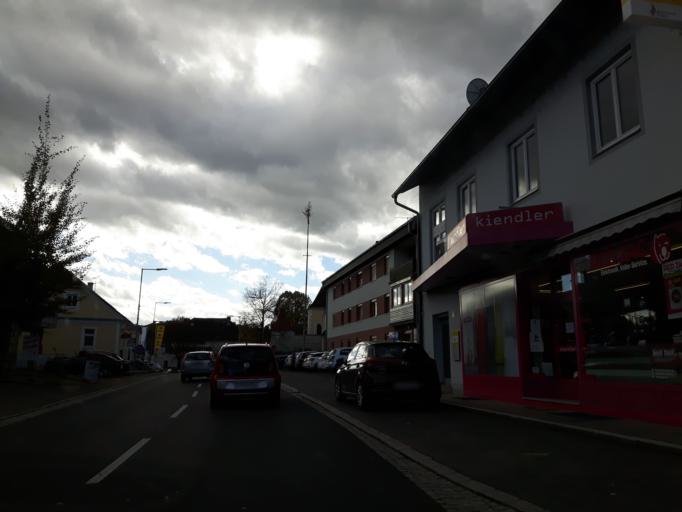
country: AT
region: Styria
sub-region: Politischer Bezirk Suedoststeiermark
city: Sankt Stefan im Rosental
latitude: 46.9056
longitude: 15.7112
